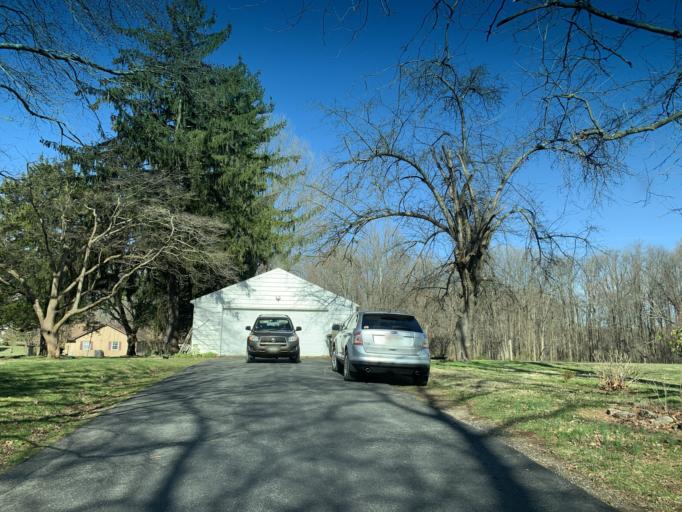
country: US
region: Maryland
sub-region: Harford County
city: Aberdeen
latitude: 39.5415
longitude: -76.2225
